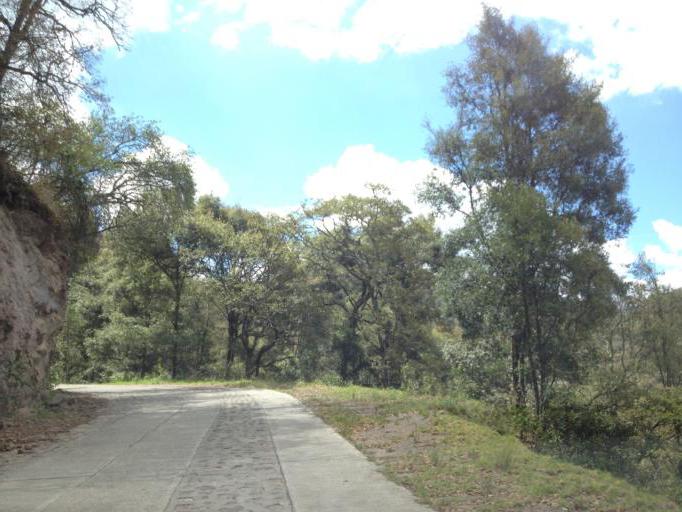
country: MX
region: Hidalgo
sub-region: Pachuca de Soto
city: San Miguel Cerezo (El Cerezo)
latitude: 20.2110
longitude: -98.6850
